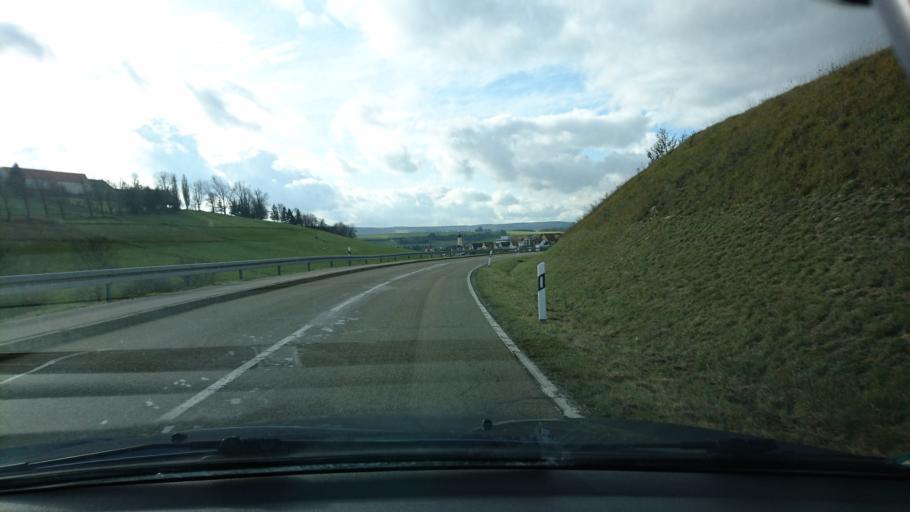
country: DE
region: Baden-Wuerttemberg
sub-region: Regierungsbezirk Stuttgart
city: Neresheim
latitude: 48.7604
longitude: 10.3435
